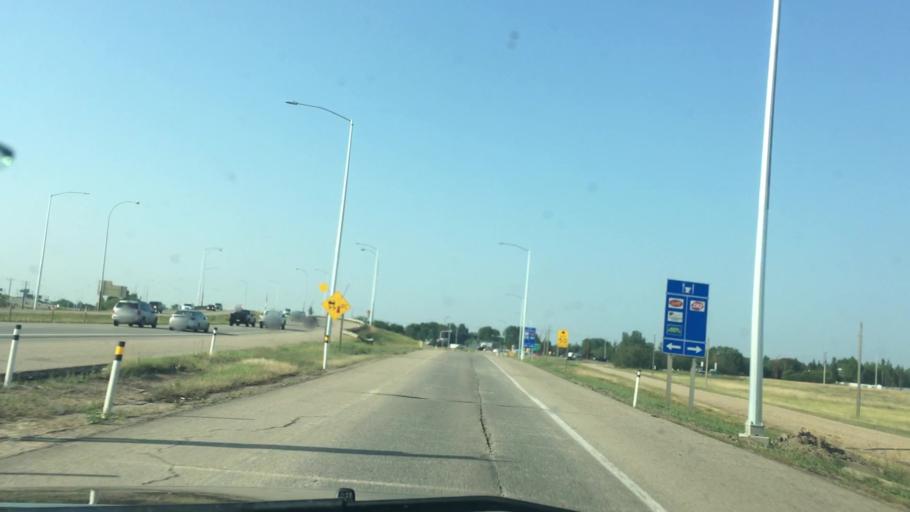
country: CA
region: Alberta
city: Leduc
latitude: 53.2680
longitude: -113.5632
